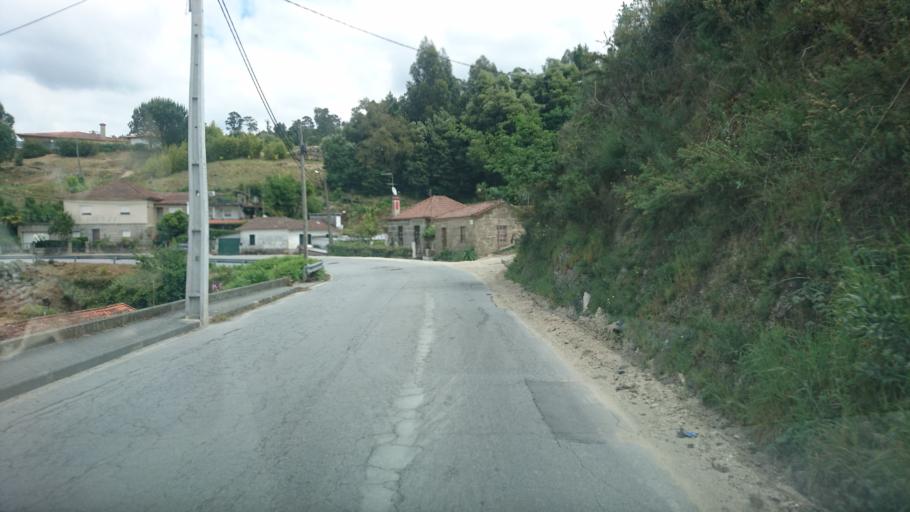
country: PT
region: Porto
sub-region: Paredes
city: Baltar
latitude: 41.1595
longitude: -8.3582
